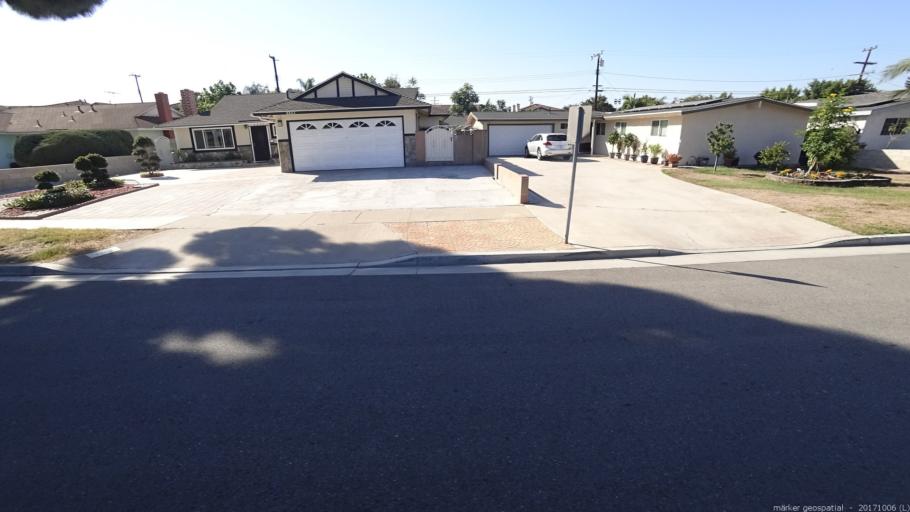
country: US
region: California
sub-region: Orange County
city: Stanton
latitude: 33.7824
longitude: -117.9775
